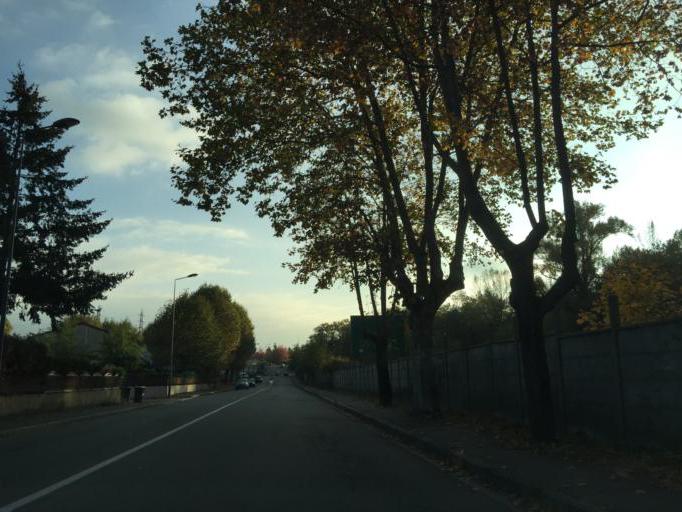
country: FR
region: Rhone-Alpes
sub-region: Departement de la Loire
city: Saint-Priest-en-Jarez
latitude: 45.4623
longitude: 4.3974
